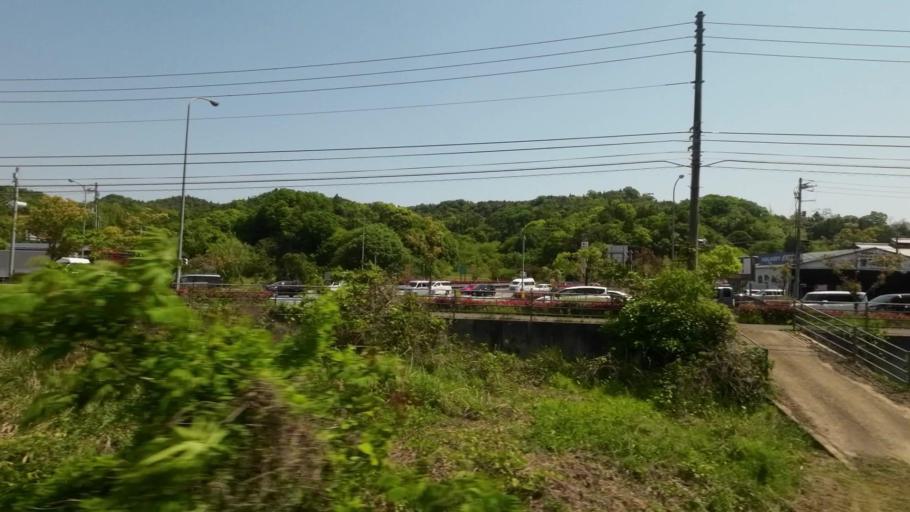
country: JP
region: Ehime
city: Saijo
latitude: 33.9963
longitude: 133.0434
